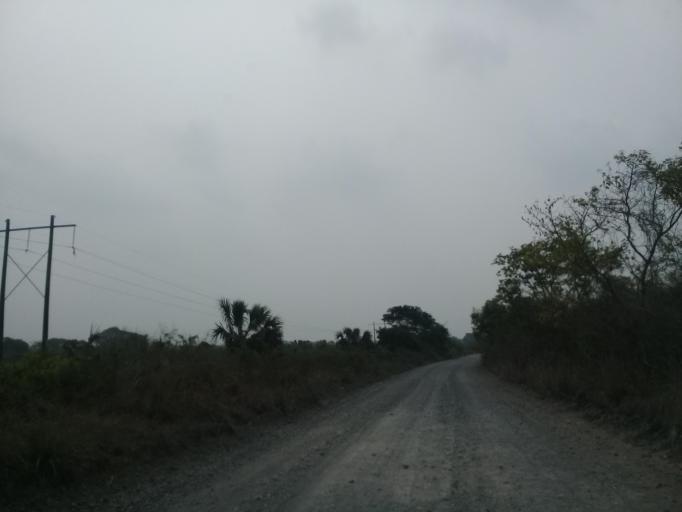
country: MX
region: Veracruz
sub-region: Medellin
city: La Laguna y Monte del Castillo
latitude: 18.9080
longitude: -96.1895
